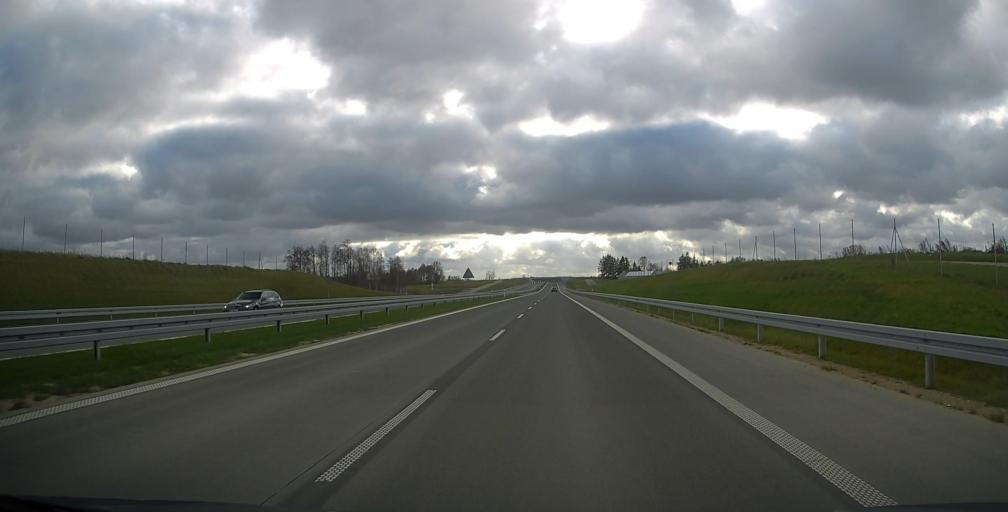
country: PL
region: Podlasie
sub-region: Powiat suwalski
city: Raczki
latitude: 53.9495
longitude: 22.7664
